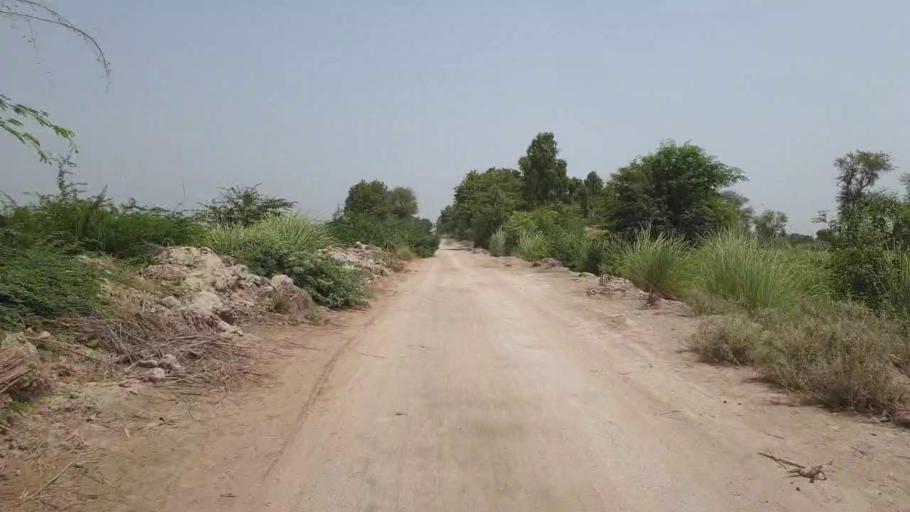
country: PK
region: Sindh
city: Nawabshah
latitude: 26.3123
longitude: 68.3009
